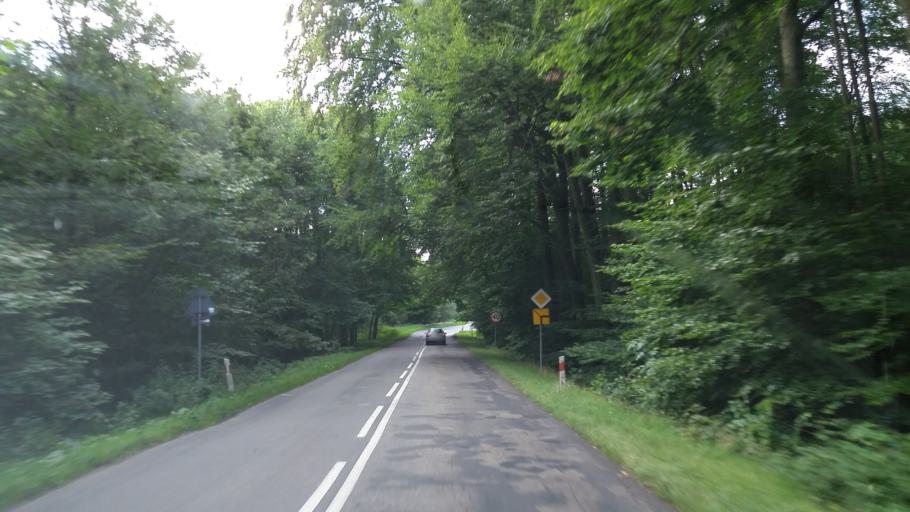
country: PL
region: West Pomeranian Voivodeship
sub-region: Powiat choszczenski
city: Pelczyce
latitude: 53.0825
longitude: 15.2831
